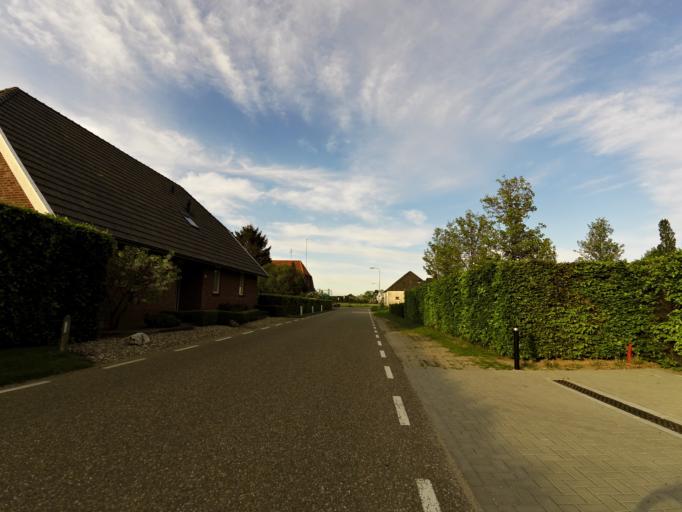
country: NL
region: Gelderland
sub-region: Oude IJsselstreek
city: Gendringen
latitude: 51.8697
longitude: 6.3549
